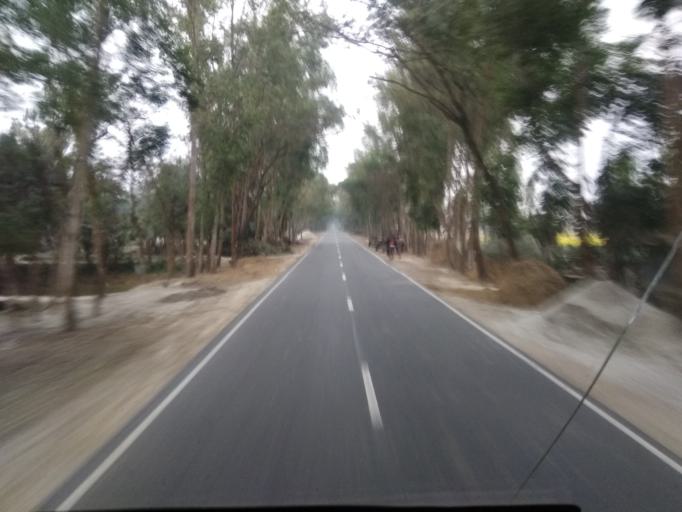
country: BD
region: Rajshahi
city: Bogra
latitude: 24.6624
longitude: 89.2694
